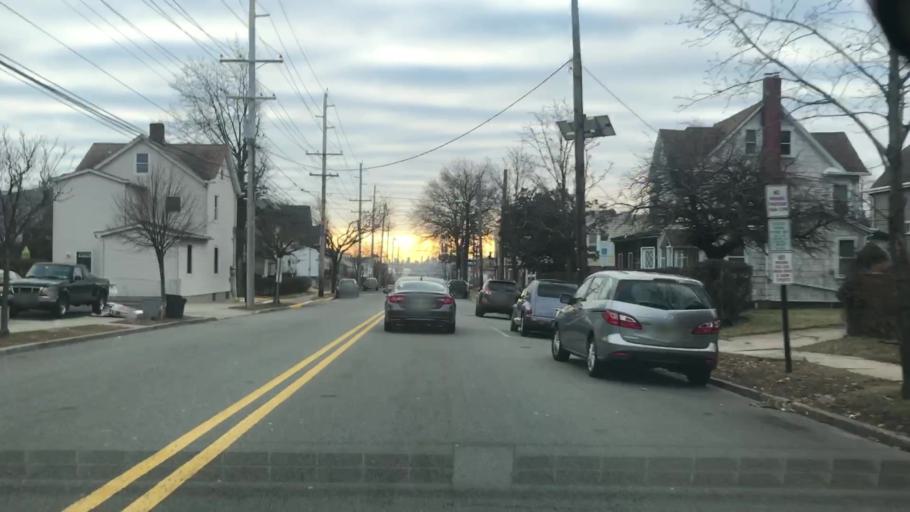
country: US
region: New Jersey
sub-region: Bergen County
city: East Rutherford
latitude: 40.8375
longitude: -74.0958
